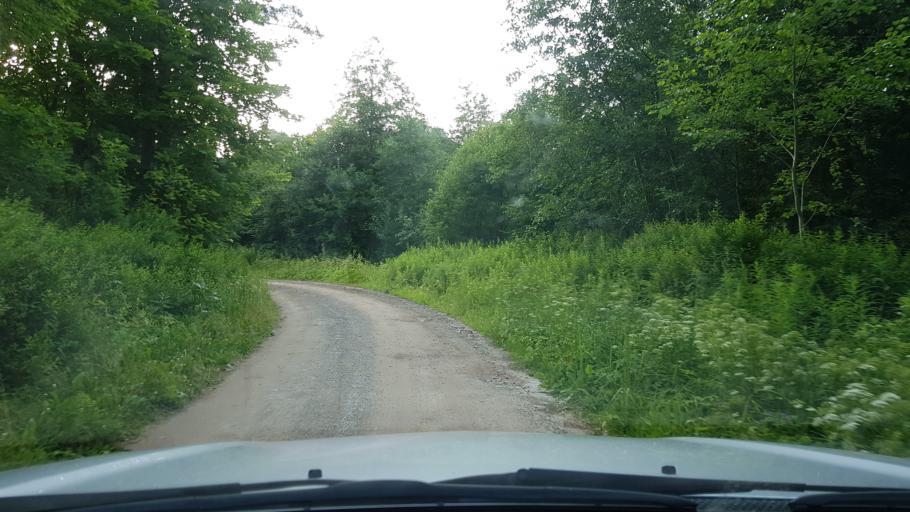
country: EE
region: Ida-Virumaa
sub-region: Narva-Joesuu linn
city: Narva-Joesuu
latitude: 59.4554
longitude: 28.0734
